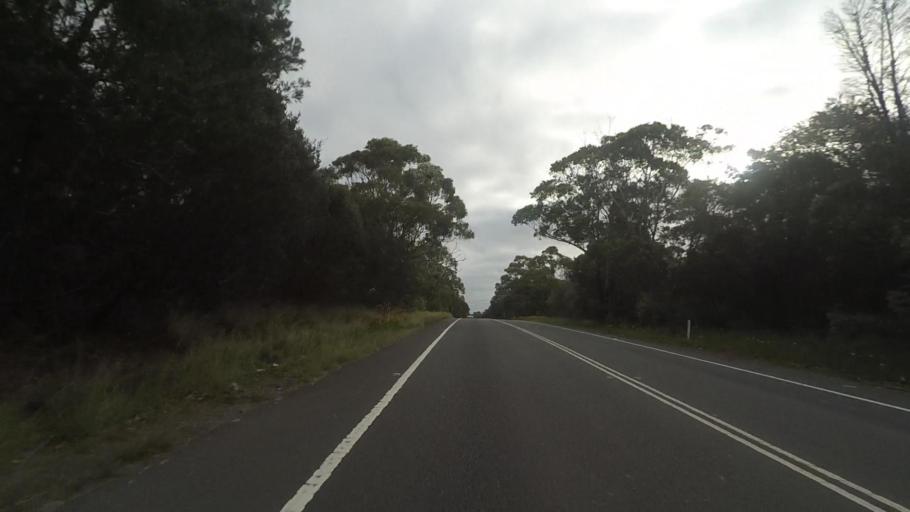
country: AU
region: New South Wales
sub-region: Sutherland Shire
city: Engadine
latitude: -34.0430
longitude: 150.9943
